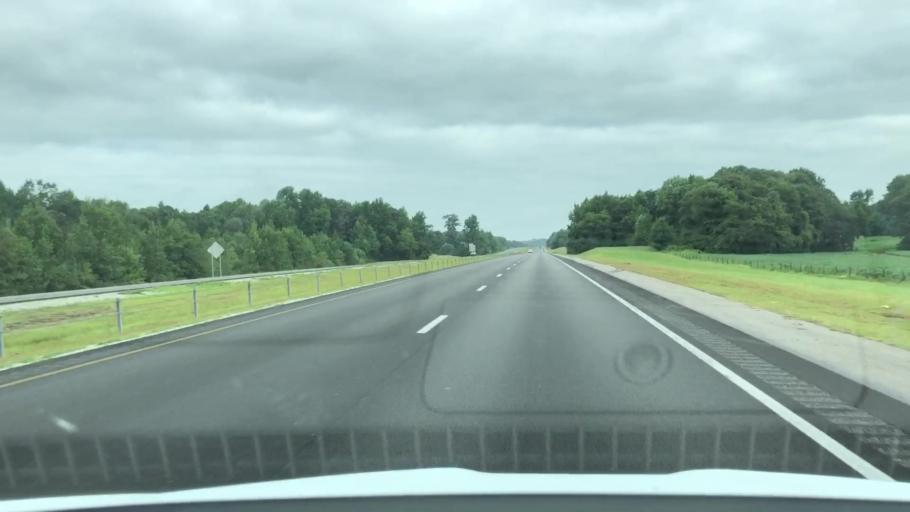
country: US
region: North Carolina
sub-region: Wayne County
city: Fremont
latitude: 35.5636
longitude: -77.9878
